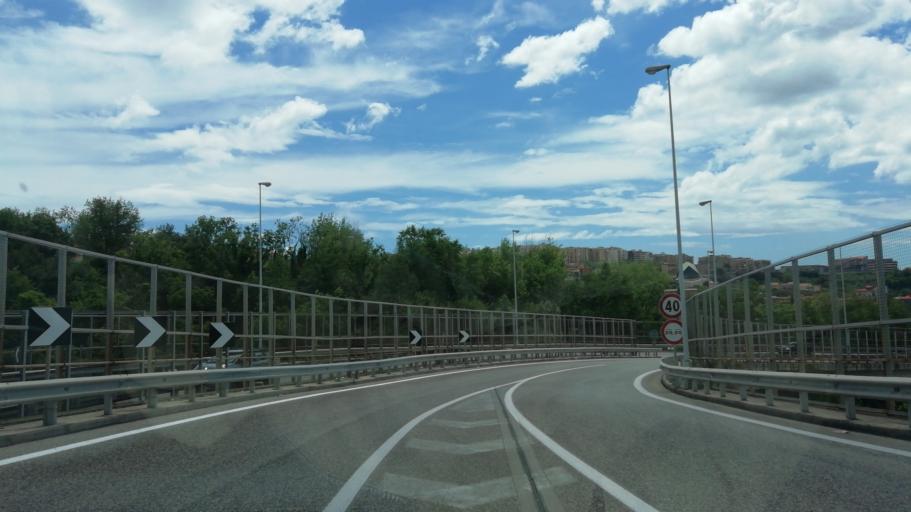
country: IT
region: Campania
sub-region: Provincia di Napoli
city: Napoli
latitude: 40.8457
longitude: 14.2123
